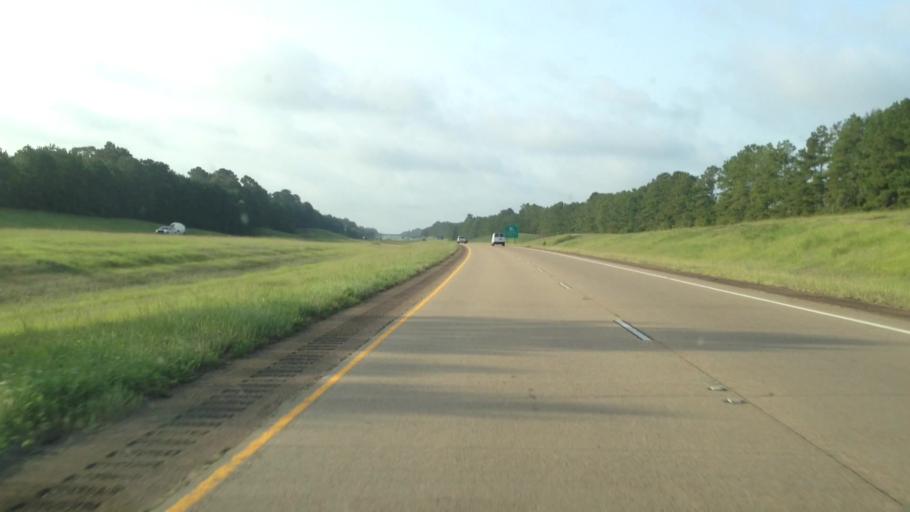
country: US
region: Louisiana
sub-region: Rapides Parish
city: Lecompte
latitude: 31.0904
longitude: -92.4440
